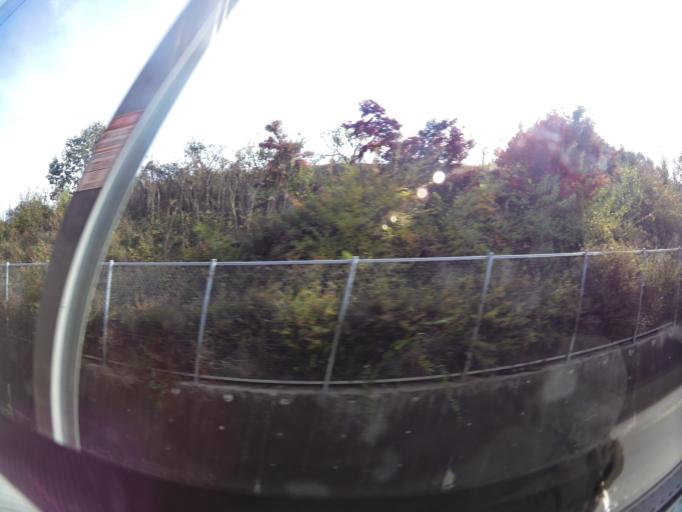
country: KR
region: Daejeon
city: Daejeon
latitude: 36.3321
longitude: 127.4780
